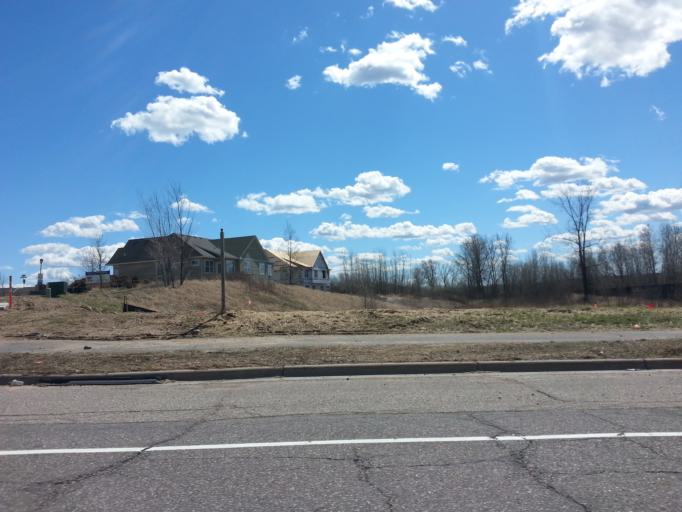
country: US
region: Minnesota
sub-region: Dakota County
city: Lakeville
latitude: 44.6814
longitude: -93.2818
